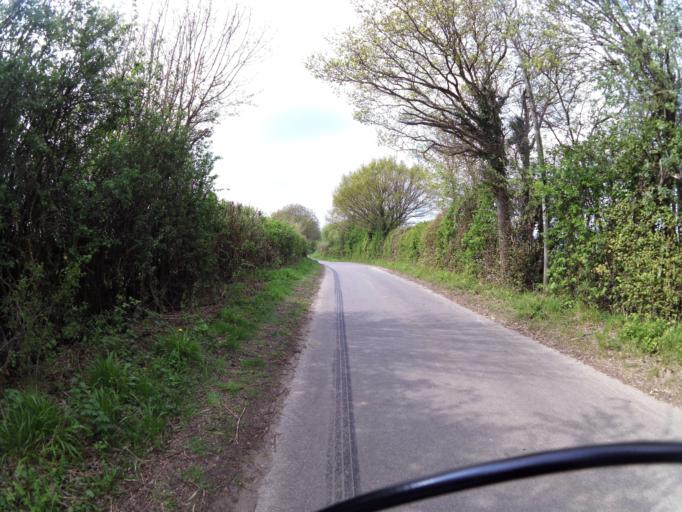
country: GB
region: England
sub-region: Suffolk
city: Hadleigh
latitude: 52.0490
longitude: 0.8802
